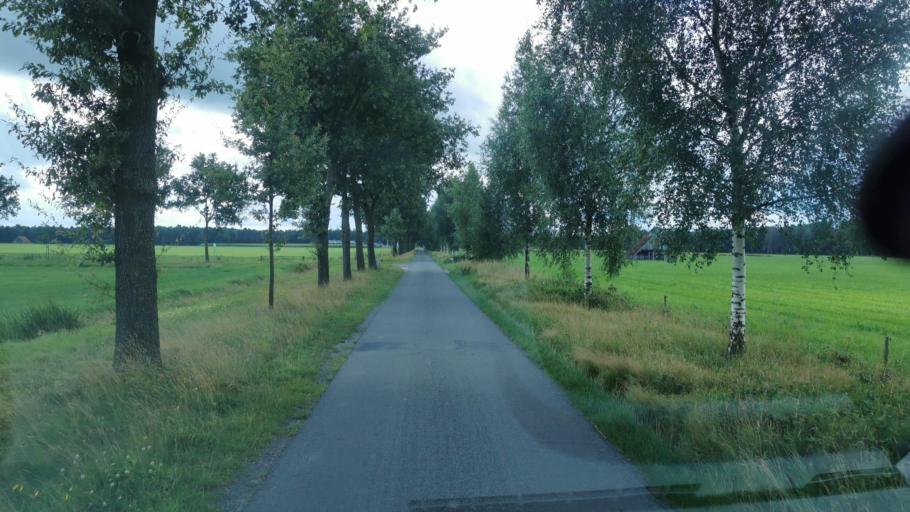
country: DE
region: North Rhine-Westphalia
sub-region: Regierungsbezirk Munster
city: Vreden
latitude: 52.1269
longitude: 6.8300
